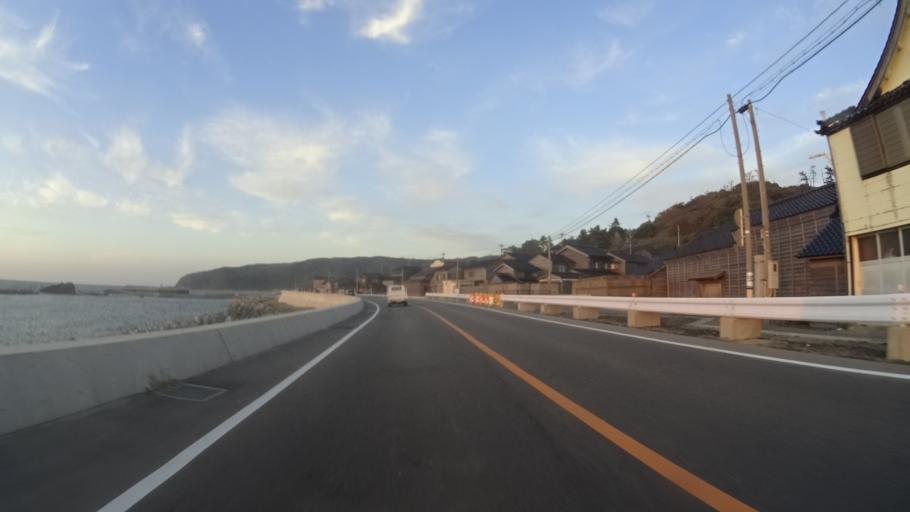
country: JP
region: Ishikawa
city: Nanao
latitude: 37.2791
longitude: 136.7338
